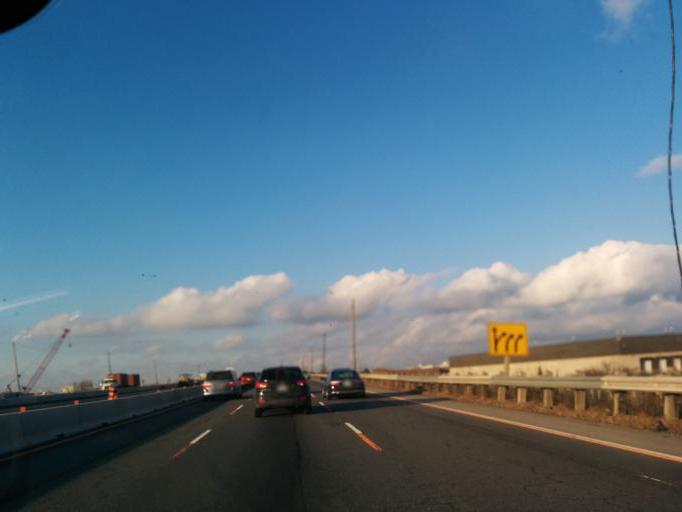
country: CA
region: Ontario
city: Etobicoke
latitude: 43.7411
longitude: -79.6284
